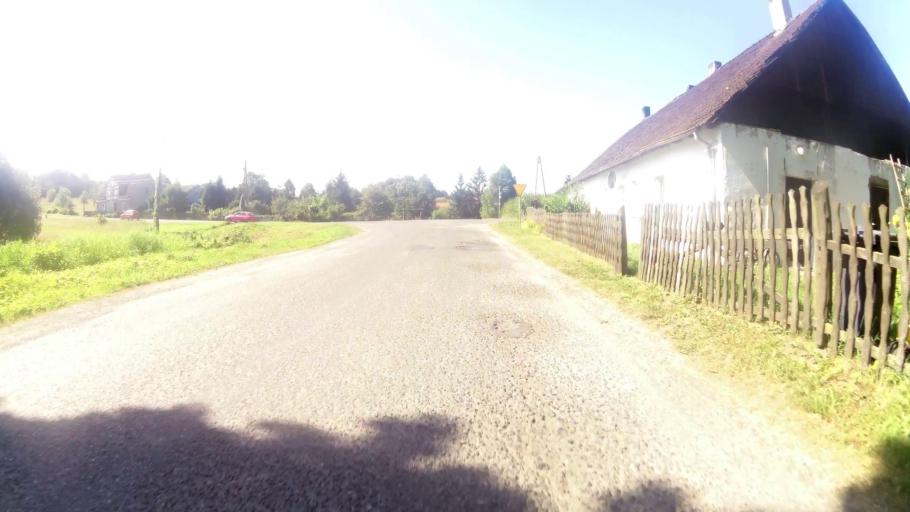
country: PL
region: West Pomeranian Voivodeship
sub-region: Powiat stargardzki
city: Insko
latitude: 53.4456
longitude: 15.6446
